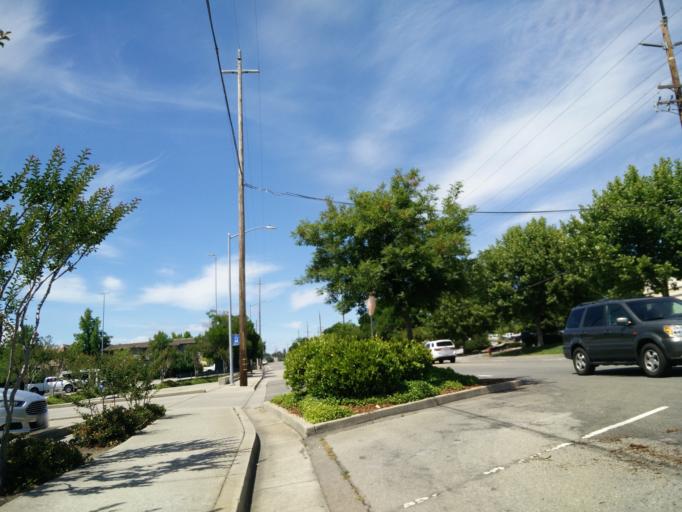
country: US
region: California
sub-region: Shasta County
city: Redding
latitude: 40.5887
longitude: -122.3535
